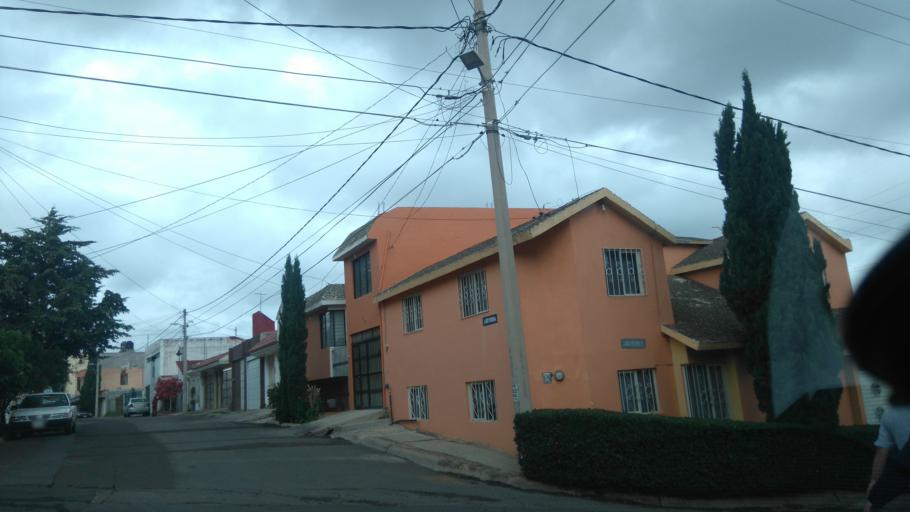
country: MX
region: Zacatecas
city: Zacatecas
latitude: 22.7562
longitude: -102.5890
